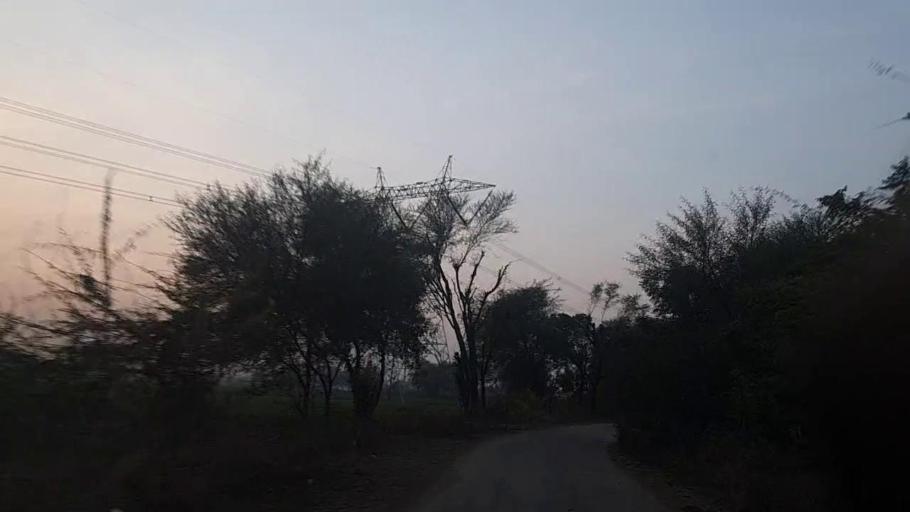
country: PK
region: Sindh
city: Sakrand
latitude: 26.0999
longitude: 68.3237
